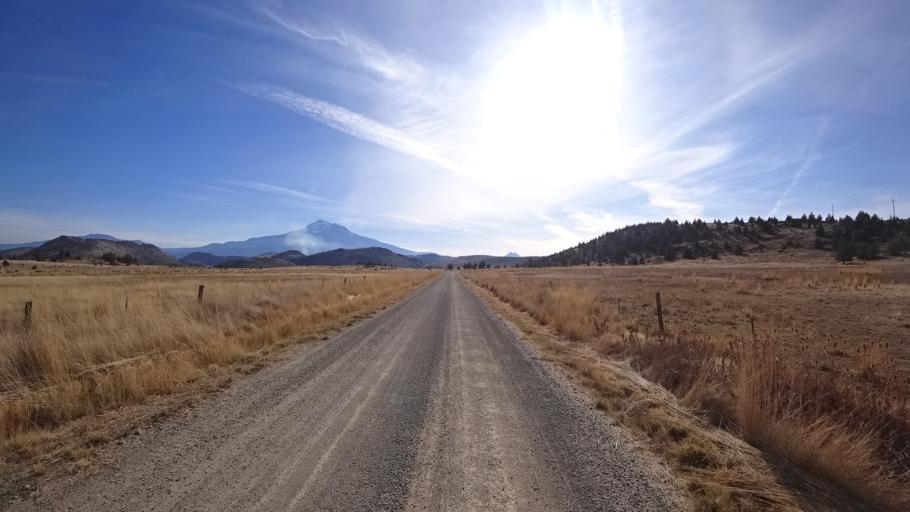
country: US
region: California
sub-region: Siskiyou County
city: Weed
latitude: 41.5407
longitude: -122.4721
